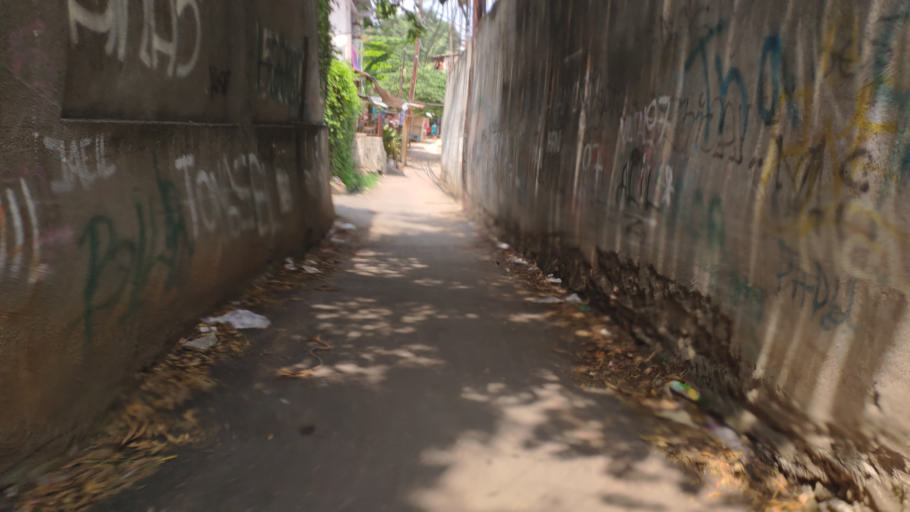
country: ID
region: Jakarta Raya
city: Jakarta
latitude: -6.2692
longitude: 106.8277
